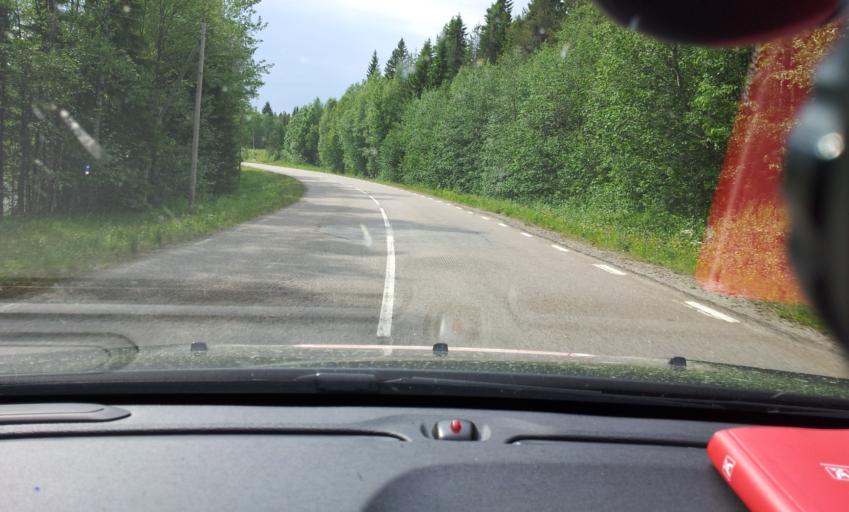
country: SE
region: Jaemtland
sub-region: OEstersunds Kommun
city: Brunflo
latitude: 62.6641
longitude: 14.8537
